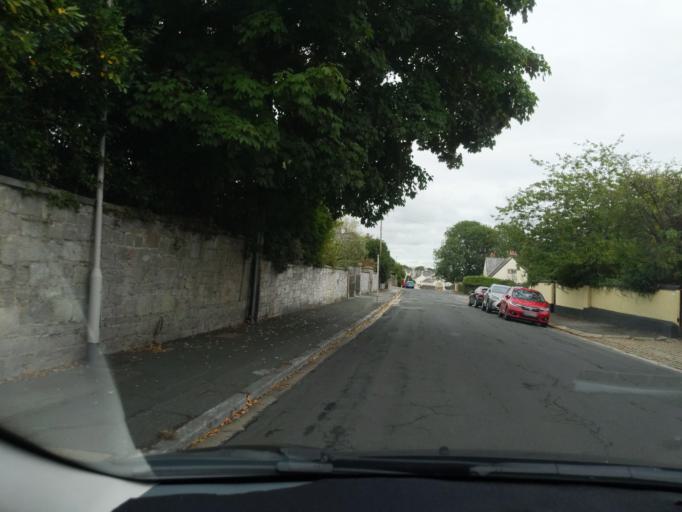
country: GB
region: England
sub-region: Plymouth
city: Plymouth
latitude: 50.3786
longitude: -4.1596
